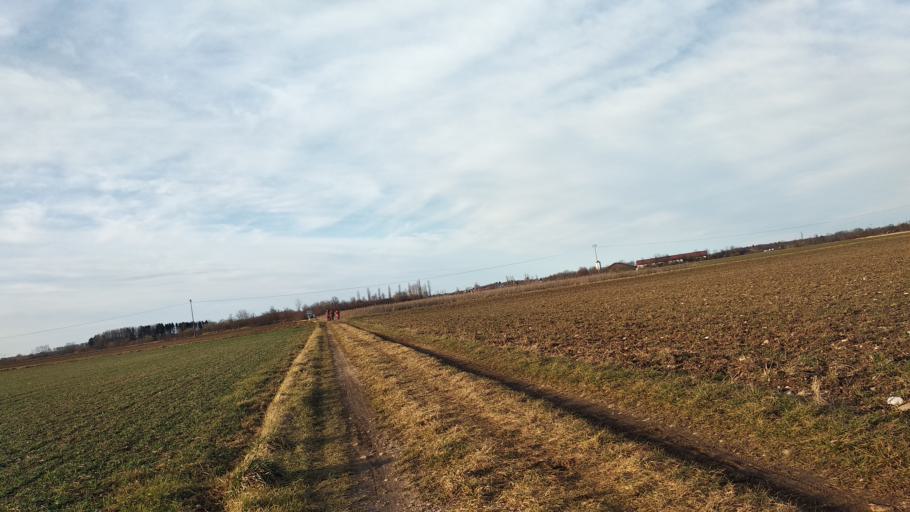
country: DE
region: Bavaria
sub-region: Upper Bavaria
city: Feldkirchen
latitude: 48.1533
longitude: 11.7186
